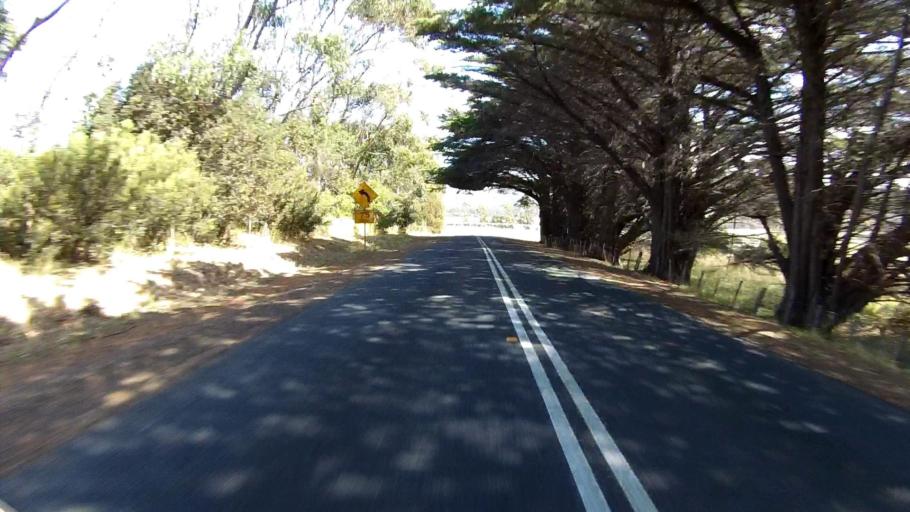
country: AU
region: Tasmania
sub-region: Sorell
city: Sorell
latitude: -42.2001
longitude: 148.0463
